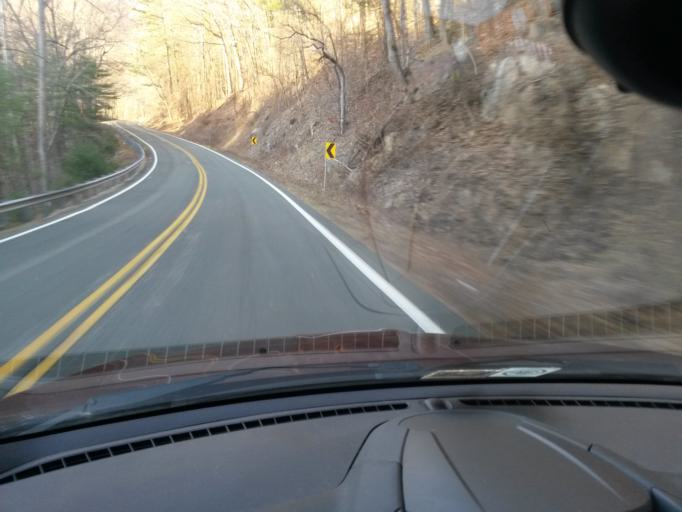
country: US
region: Virginia
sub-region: City of Buena Vista
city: Buena Vista
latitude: 37.7468
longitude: -79.2735
